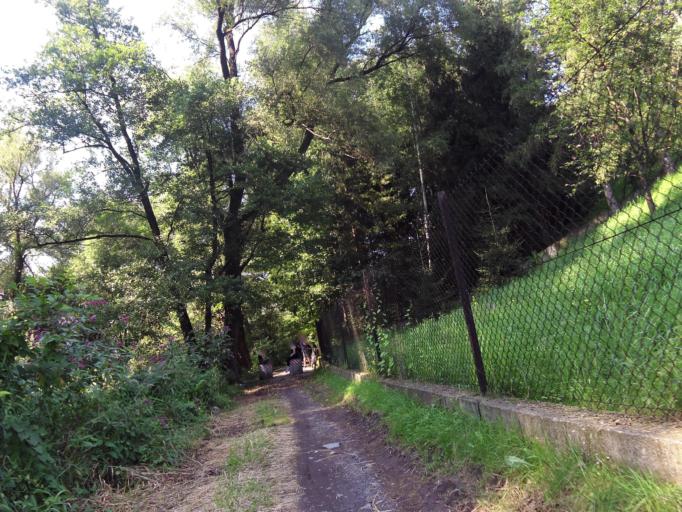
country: PL
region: Silesian Voivodeship
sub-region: Powiat zywiecki
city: Wieprz
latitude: 49.6559
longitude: 19.1816
